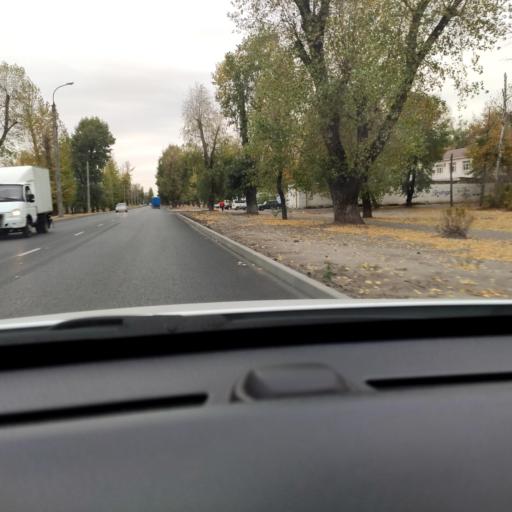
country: RU
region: Voronezj
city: Voronezh
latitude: 51.6529
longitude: 39.2464
